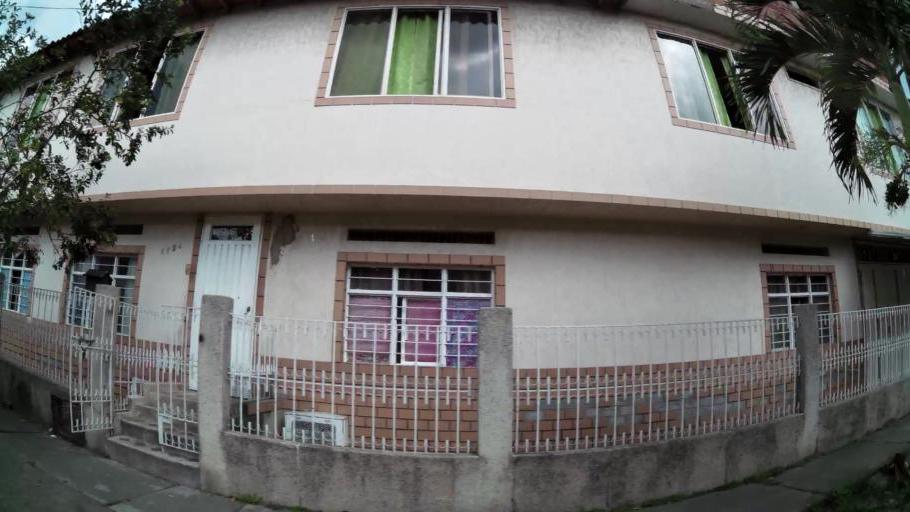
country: CO
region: Valle del Cauca
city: Cali
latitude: 3.4861
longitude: -76.5000
